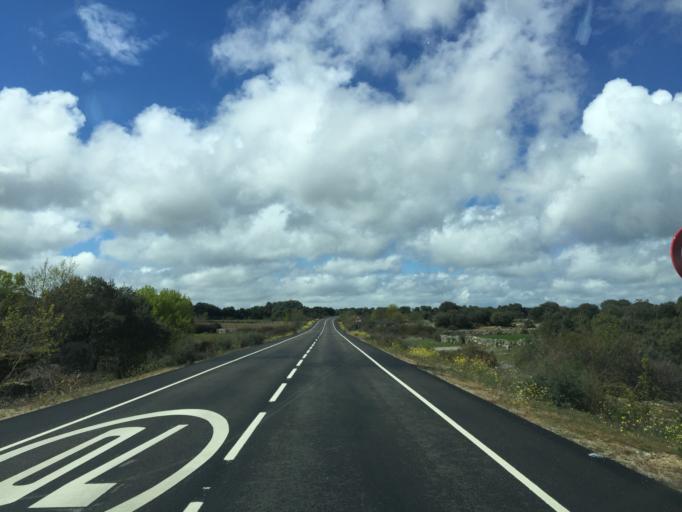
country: ES
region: Castille and Leon
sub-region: Provincia de Zamora
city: Moralina
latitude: 41.4804
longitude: -6.1408
